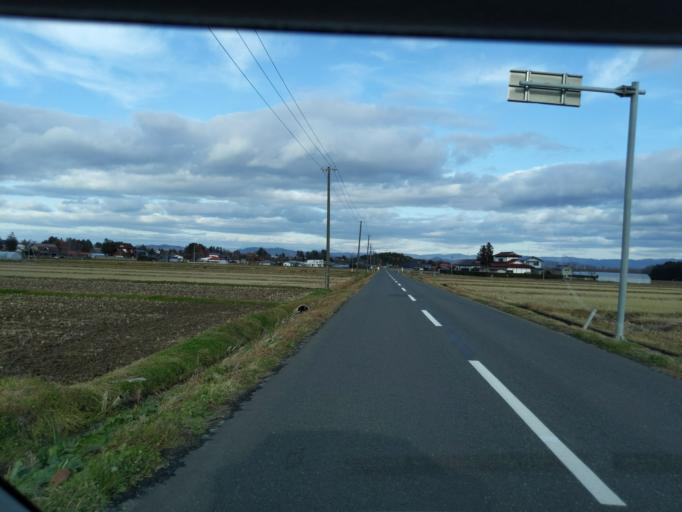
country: JP
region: Iwate
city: Mizusawa
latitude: 39.1775
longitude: 141.0978
